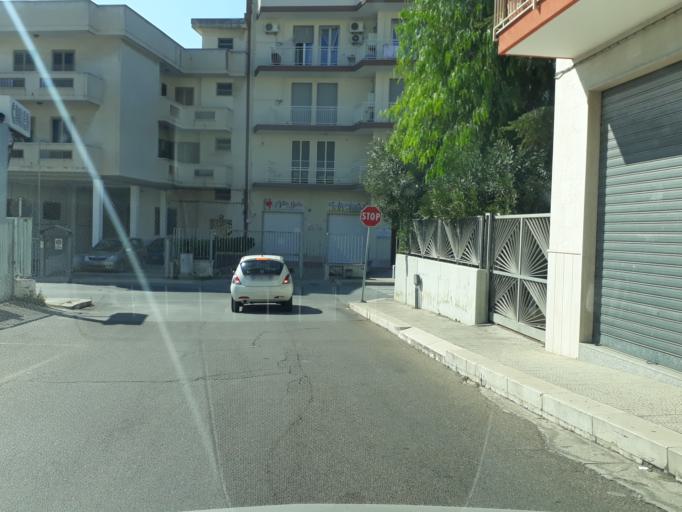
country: IT
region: Apulia
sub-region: Provincia di Bari
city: Monopoli
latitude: 40.9471
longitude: 17.2933
